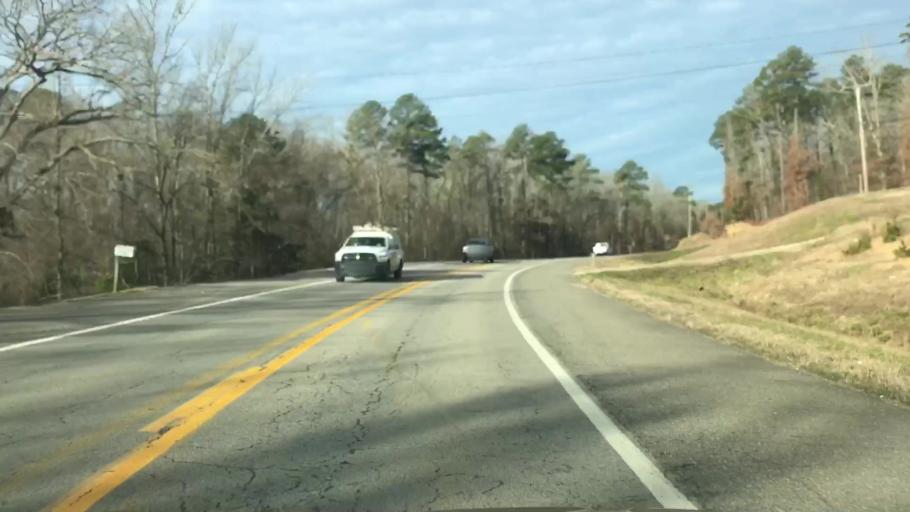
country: US
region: Arkansas
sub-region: Montgomery County
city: Mount Ida
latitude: 34.5392
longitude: -93.6028
